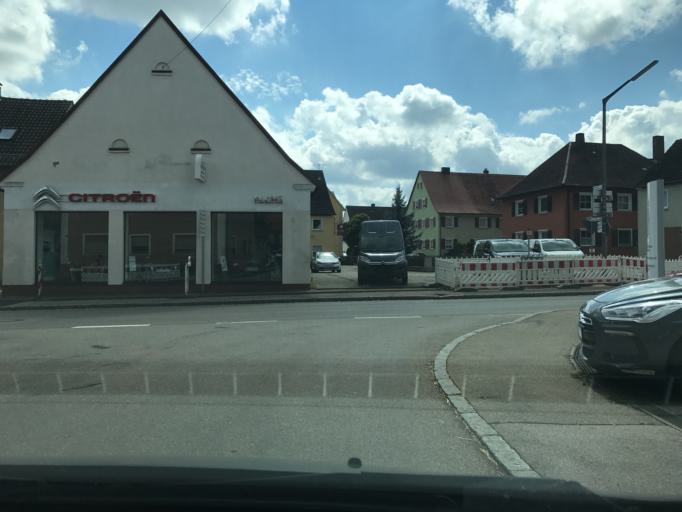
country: DE
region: Bavaria
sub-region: Regierungsbezirk Mittelfranken
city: Wittelshofen
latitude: 49.0607
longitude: 10.4815
